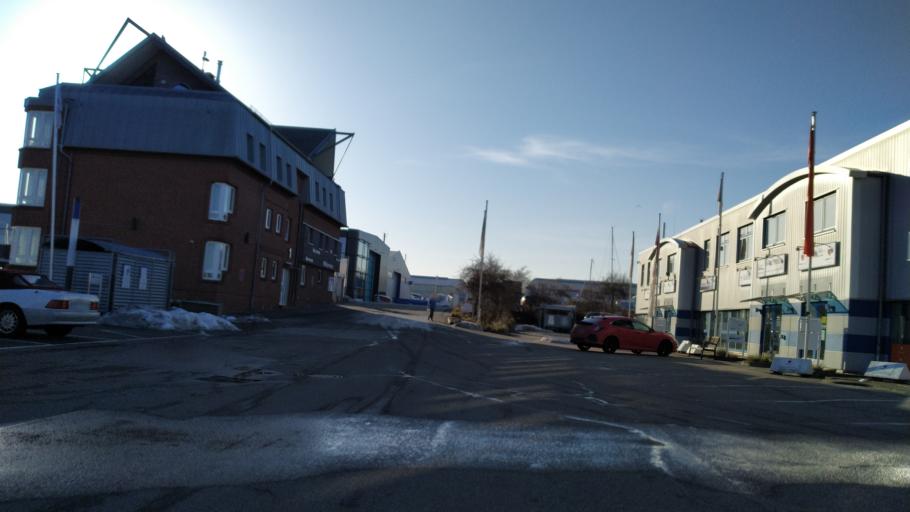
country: DE
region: Schleswig-Holstein
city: Neustadt in Holstein
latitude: 54.0941
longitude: 10.8001
